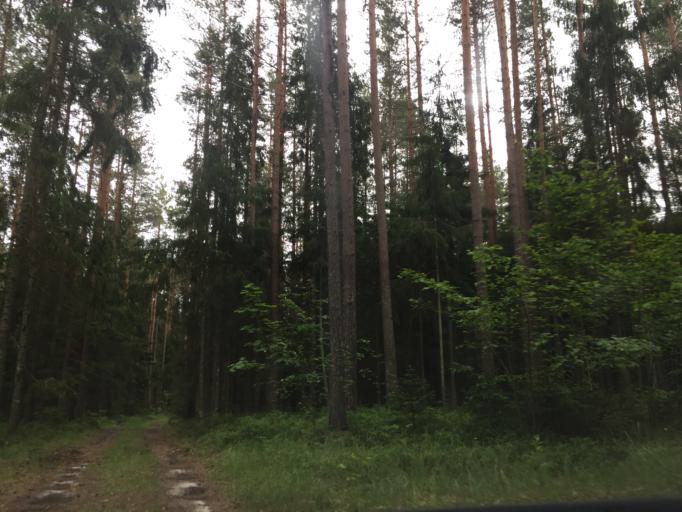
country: LV
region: Tukuma Rajons
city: Tukums
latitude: 57.0215
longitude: 23.0782
